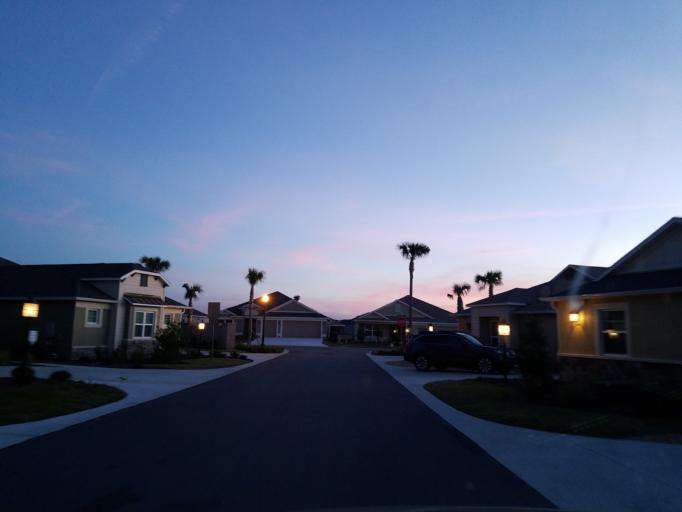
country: US
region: Florida
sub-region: Sumter County
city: Wildwood
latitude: 28.7980
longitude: -82.0316
